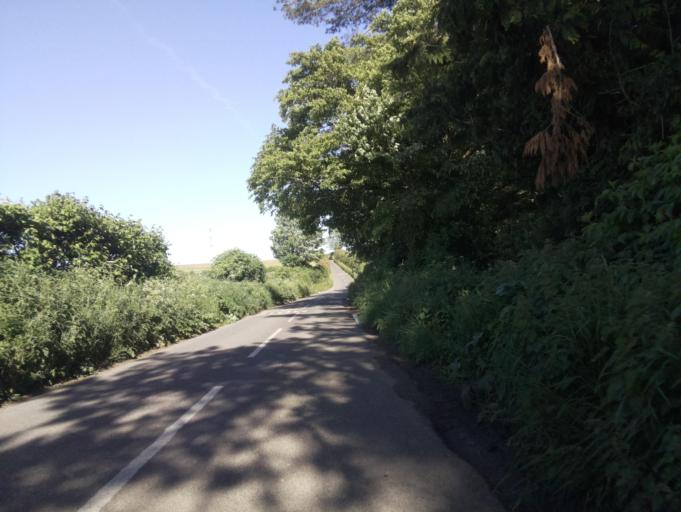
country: GB
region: England
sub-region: Somerset
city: Yeovil
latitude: 50.9337
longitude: -2.5852
